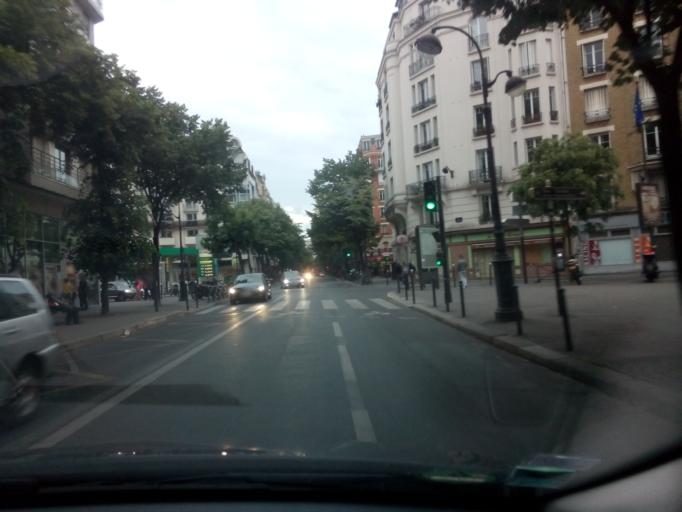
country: FR
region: Ile-de-France
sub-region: Departement des Hauts-de-Seine
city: Vanves
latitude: 48.8398
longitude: 2.2910
